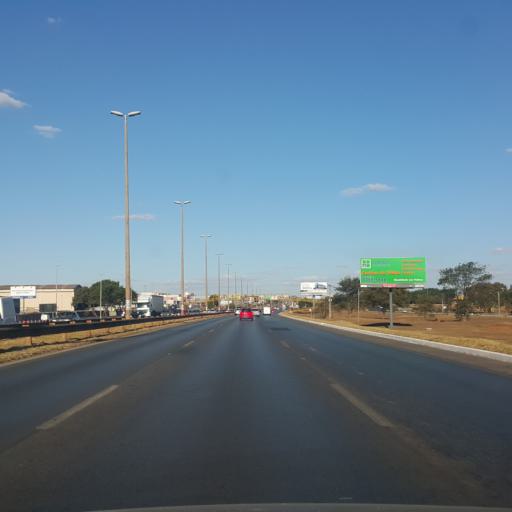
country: BR
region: Federal District
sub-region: Brasilia
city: Brasilia
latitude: -15.7889
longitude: -47.9842
